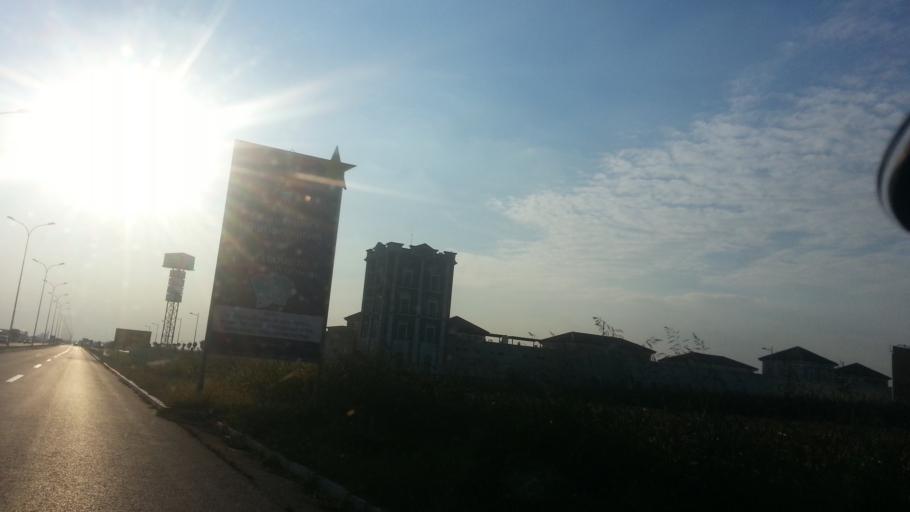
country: RS
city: Novi Karlovci
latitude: 45.0682
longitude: 20.1394
